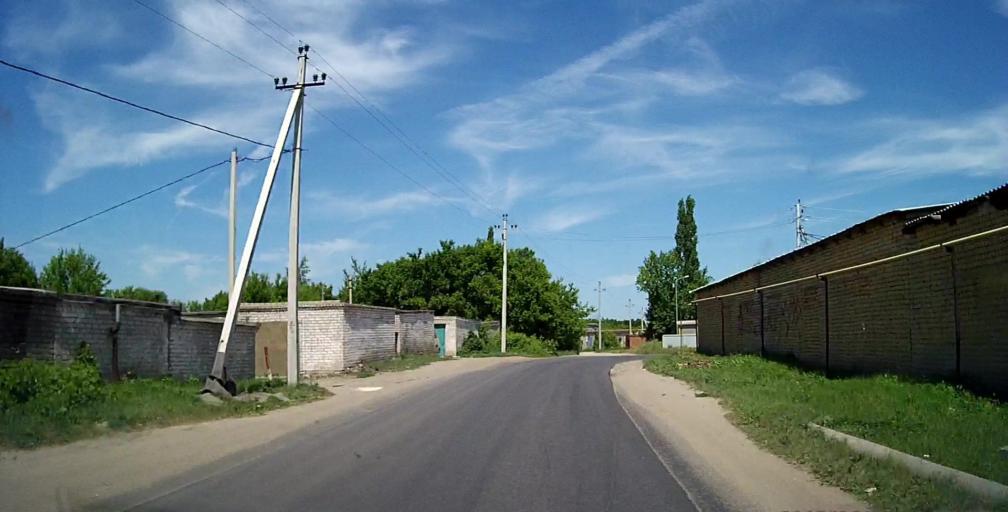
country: RU
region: Lipetsk
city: Chaplygin
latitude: 53.2484
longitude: 39.9732
